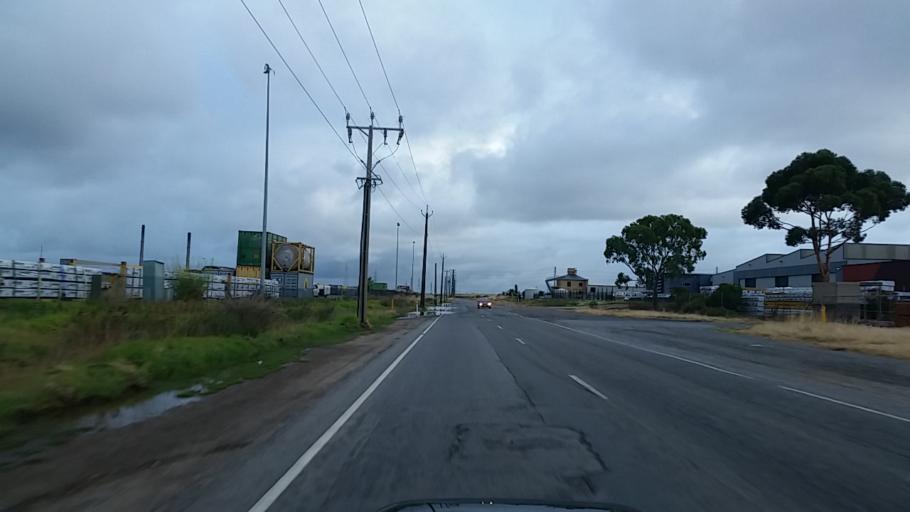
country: AU
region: South Australia
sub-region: Port Adelaide Enfield
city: Birkenhead
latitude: -34.8254
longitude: 138.5205
